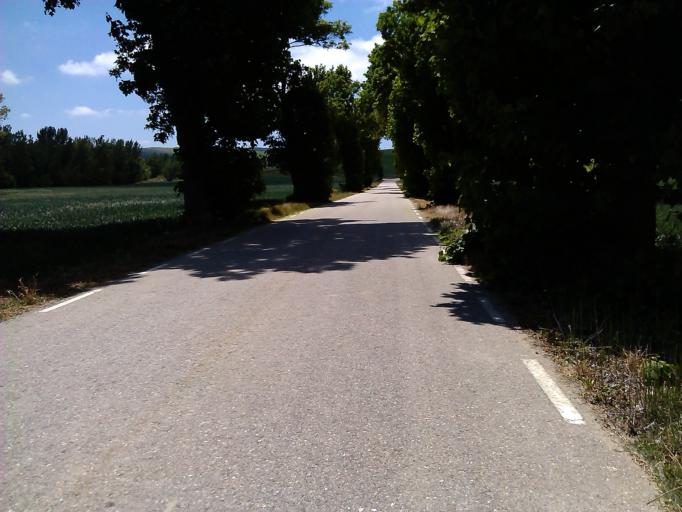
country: ES
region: Castille and Leon
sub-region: Provincia de Burgos
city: Cerraton de Juarros
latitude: 42.4379
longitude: -3.3523
